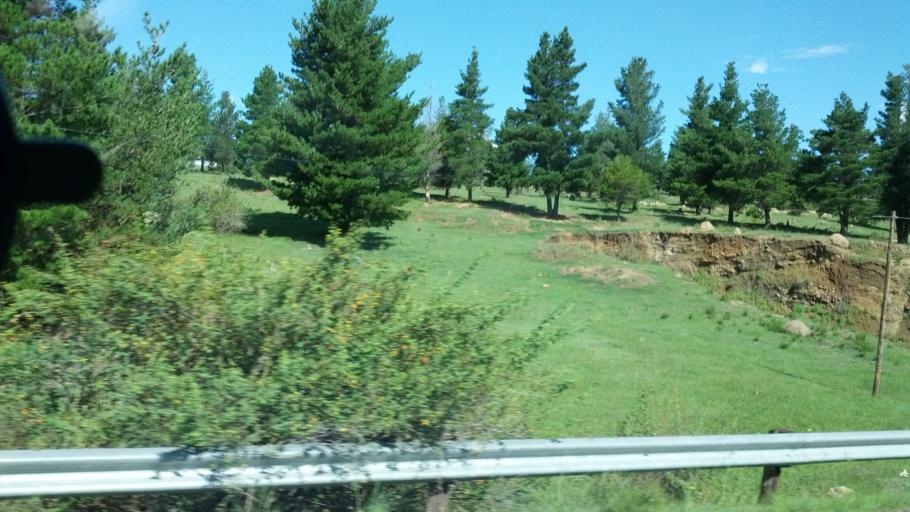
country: LS
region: Maseru
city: Maseru
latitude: -29.5190
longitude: 27.5237
